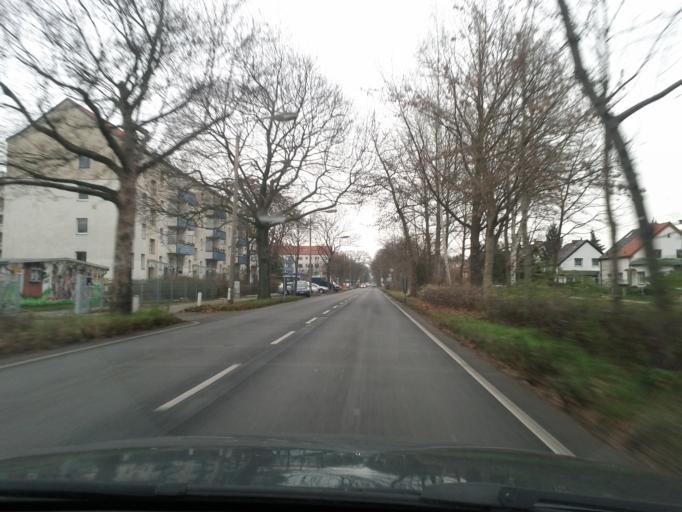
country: DE
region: Berlin
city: Oberschoneweide
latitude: 52.4514
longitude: 13.5366
